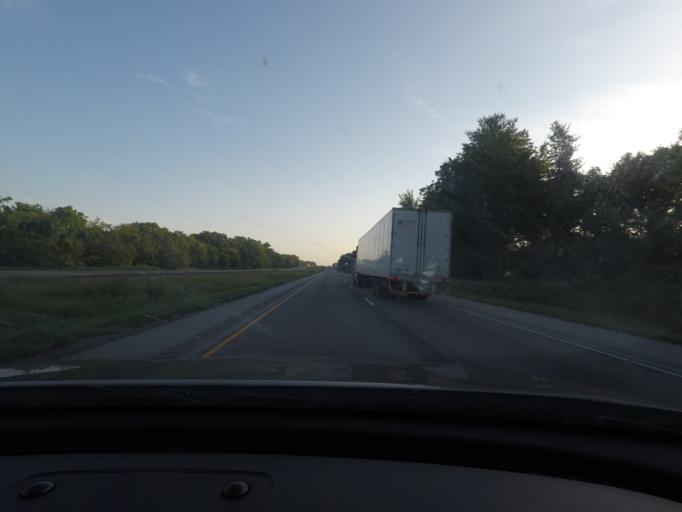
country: US
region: Illinois
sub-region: Williamson County
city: Johnston City
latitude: 37.8450
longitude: -88.9438
